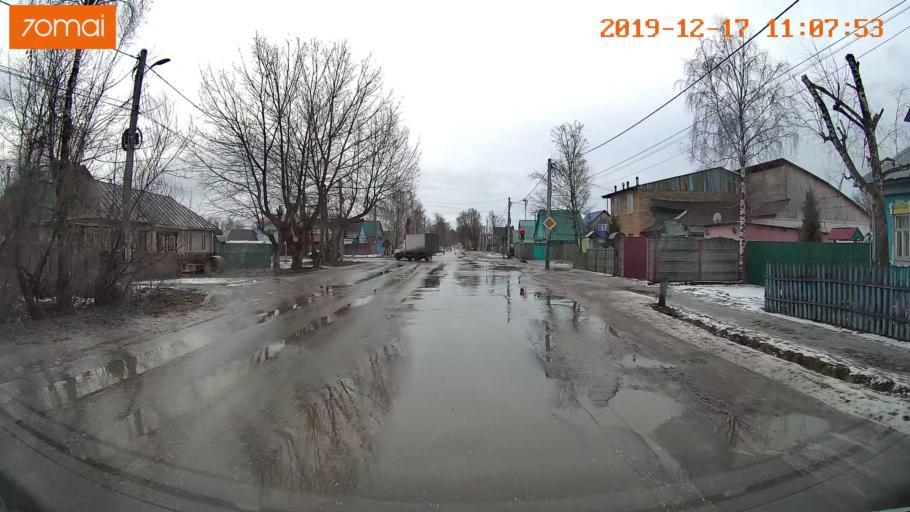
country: RU
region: Vladimir
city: Gus'-Khrustal'nyy
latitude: 55.6083
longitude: 40.6434
